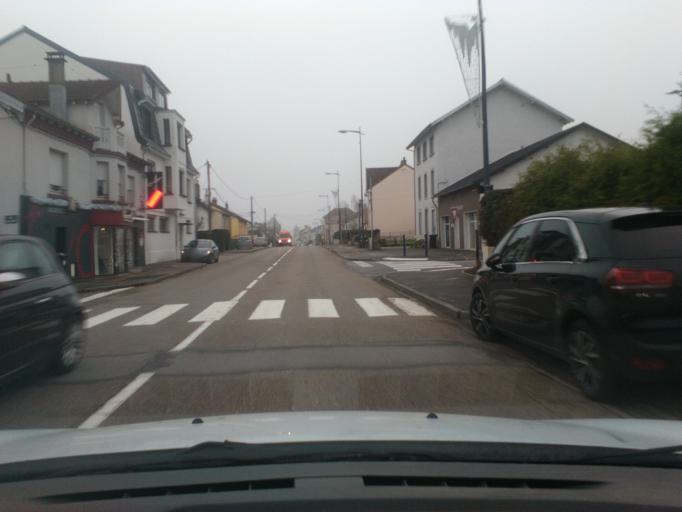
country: FR
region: Lorraine
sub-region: Departement des Vosges
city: Golbey
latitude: 48.2029
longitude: 6.4396
